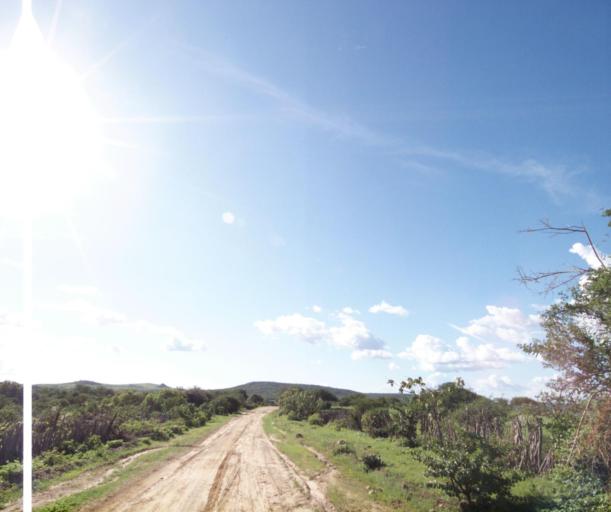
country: BR
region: Bahia
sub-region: Tanhacu
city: Tanhacu
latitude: -14.1876
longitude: -40.9456
